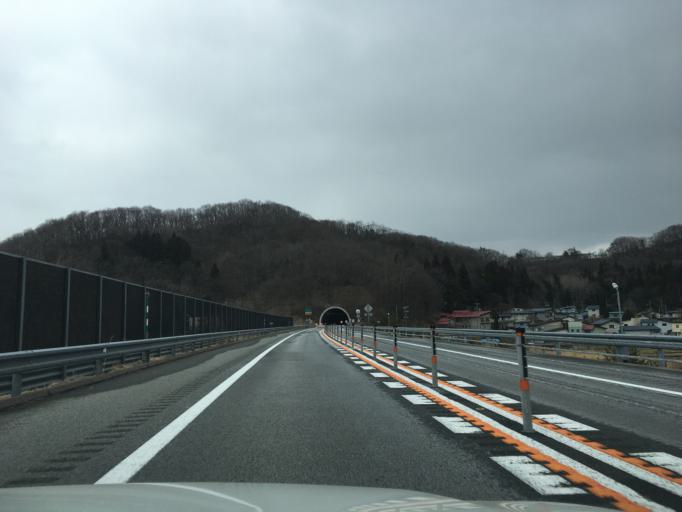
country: JP
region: Aomori
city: Aomori Shi
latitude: 40.8148
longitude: 140.8078
